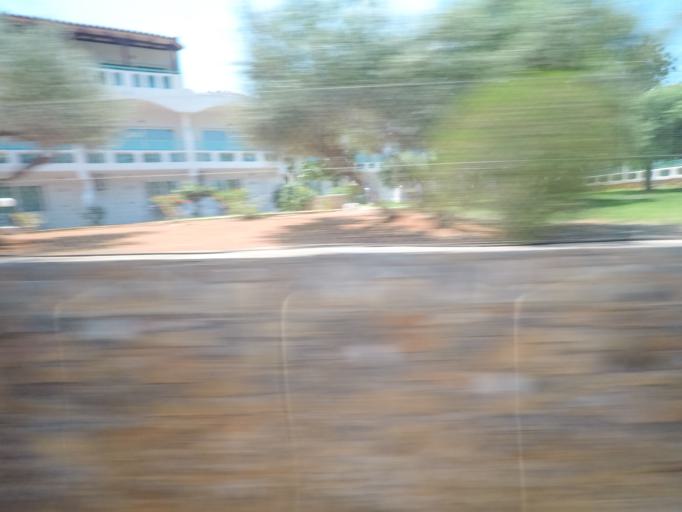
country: GR
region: Crete
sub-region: Nomos Lasithiou
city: Skhisma
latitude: 35.2457
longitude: 25.7299
